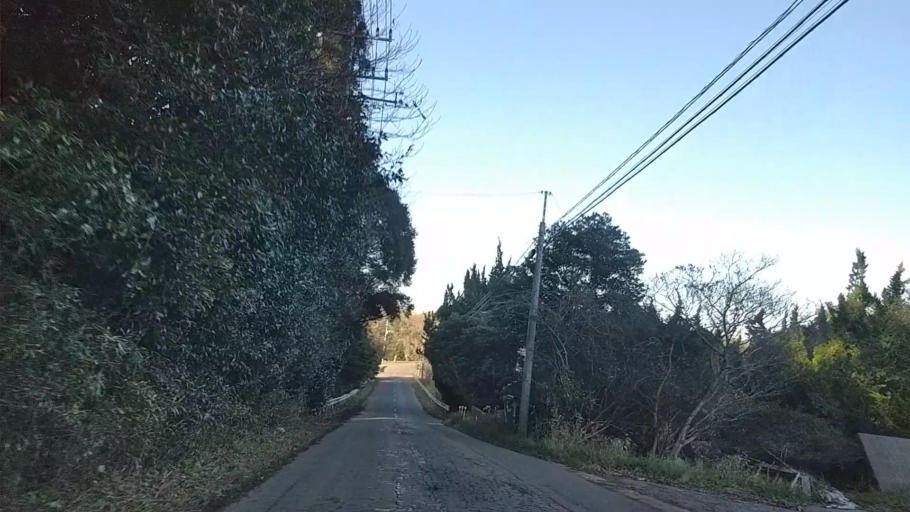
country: JP
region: Chiba
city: Asahi
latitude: 35.7243
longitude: 140.7359
